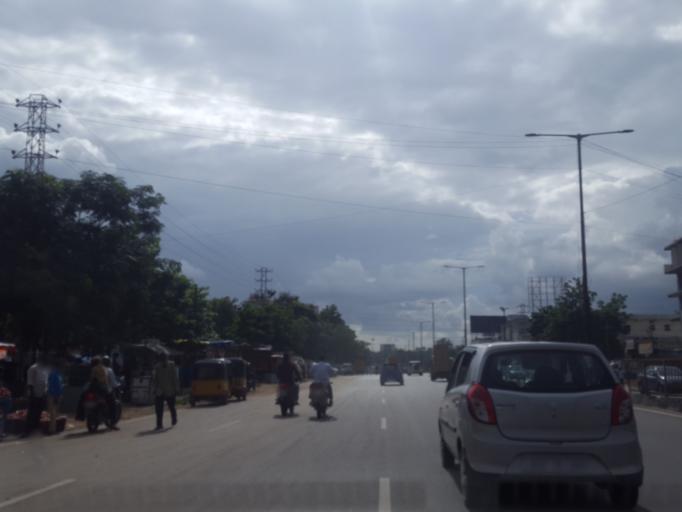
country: IN
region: Telangana
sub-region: Medak
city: Serilingampalle
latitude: 17.4950
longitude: 78.3207
